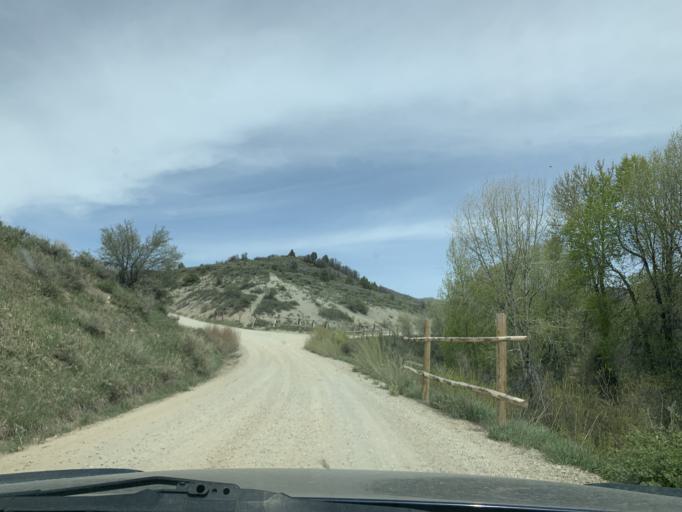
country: US
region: Utah
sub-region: Utah County
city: Mapleton
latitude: 40.1778
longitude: -111.3294
